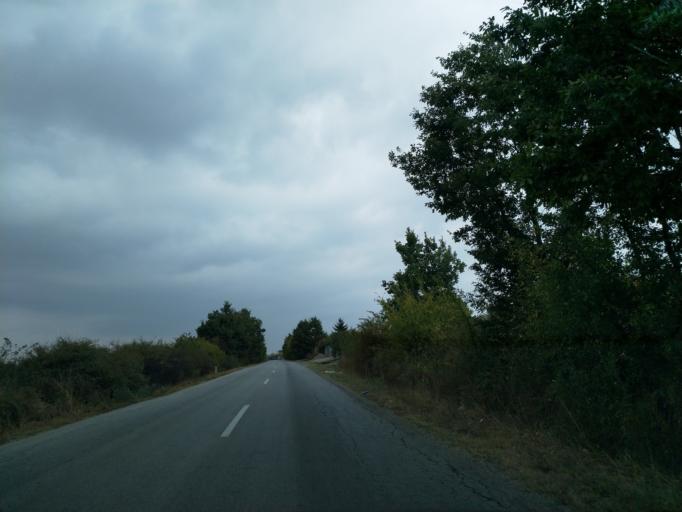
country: RS
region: Central Serbia
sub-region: Pomoravski Okrug
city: Jagodina
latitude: 44.0138
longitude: 21.1999
